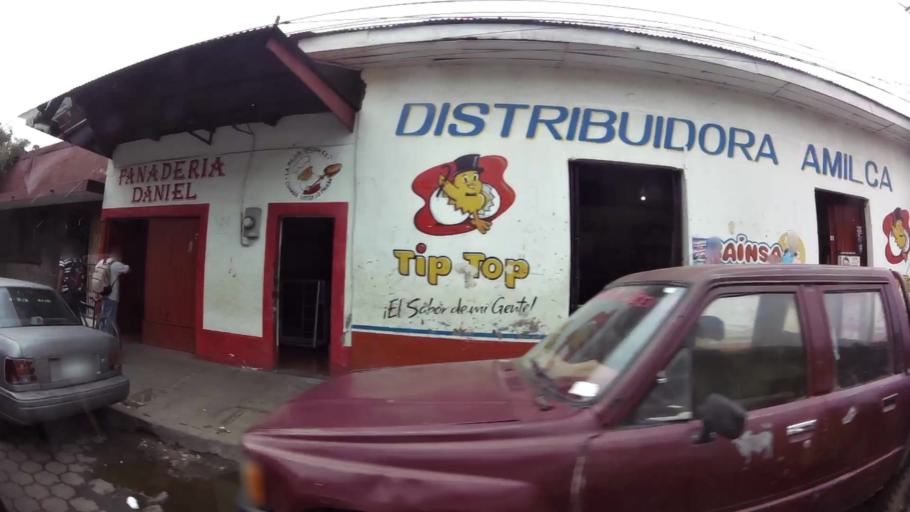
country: NI
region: Leon
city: Leon
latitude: 12.4400
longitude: -86.8731
